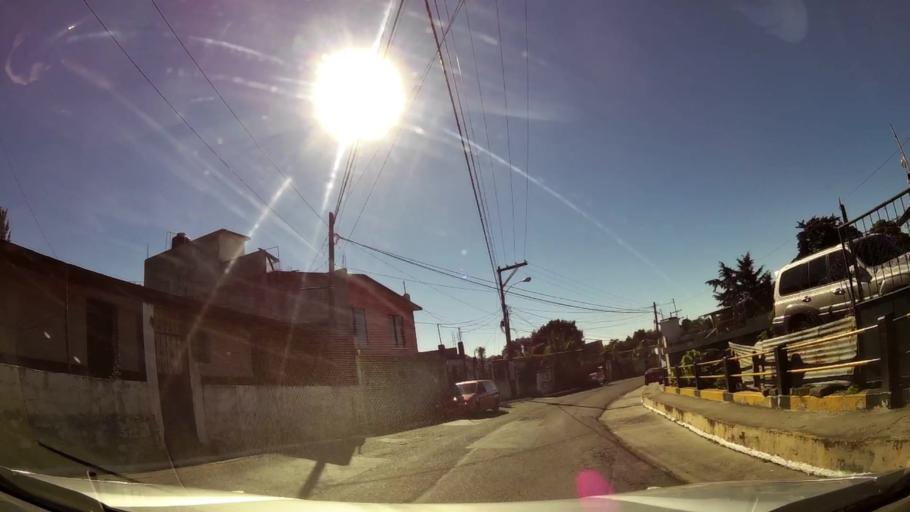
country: GT
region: Guatemala
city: Fraijanes
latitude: 14.4706
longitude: -90.4462
